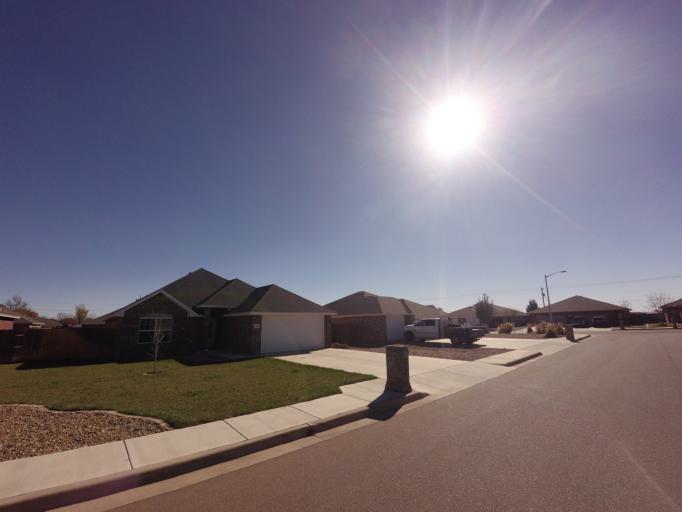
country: US
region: New Mexico
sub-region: Curry County
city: Clovis
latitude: 34.4135
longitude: -103.1713
